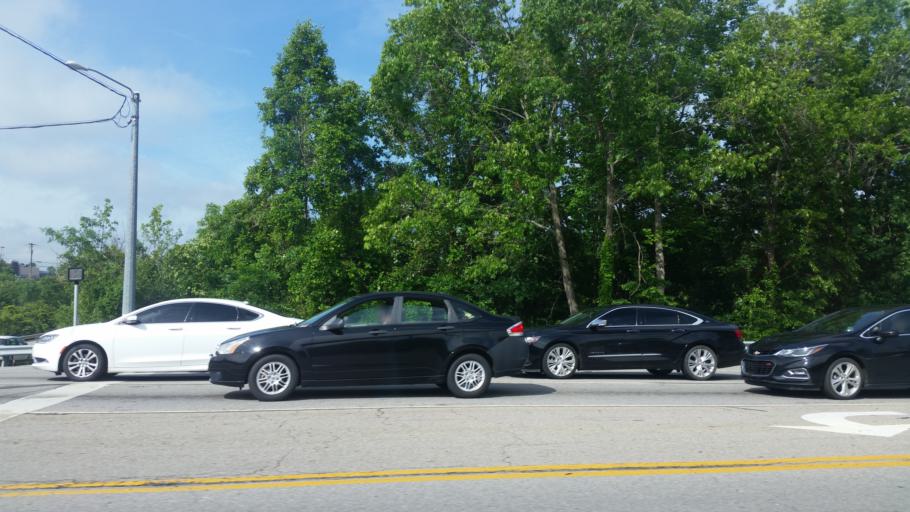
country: US
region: Kentucky
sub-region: Rowan County
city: Morehead
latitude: 38.1947
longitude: -83.4807
